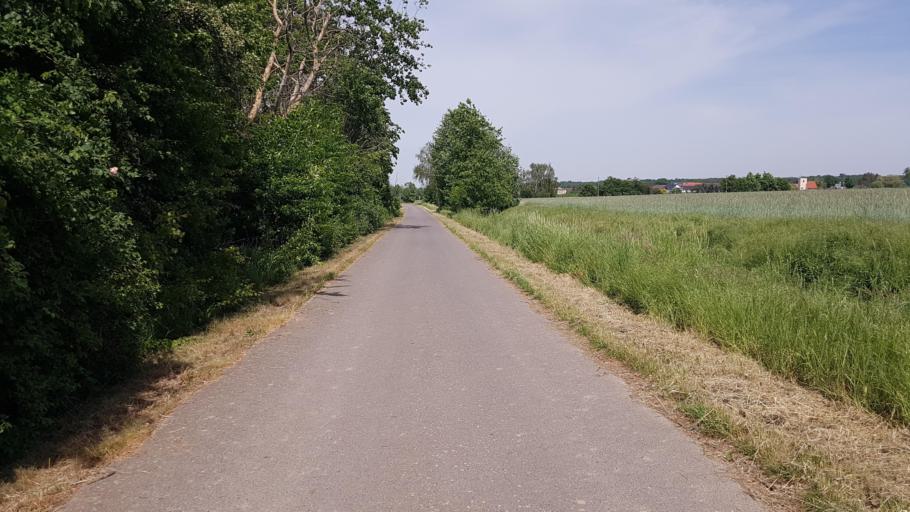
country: DE
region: Brandenburg
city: Grosskmehlen
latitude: 51.3784
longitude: 13.7086
